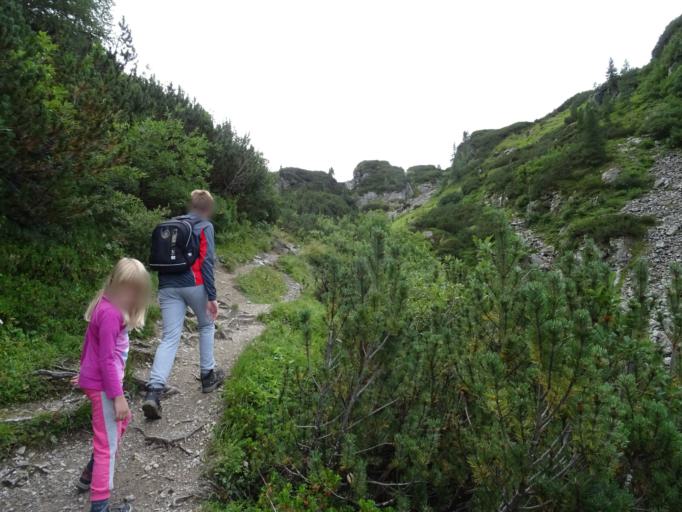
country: AT
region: Salzburg
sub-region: Politischer Bezirk Sankt Johann im Pongau
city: Untertauern
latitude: 47.2874
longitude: 13.5963
